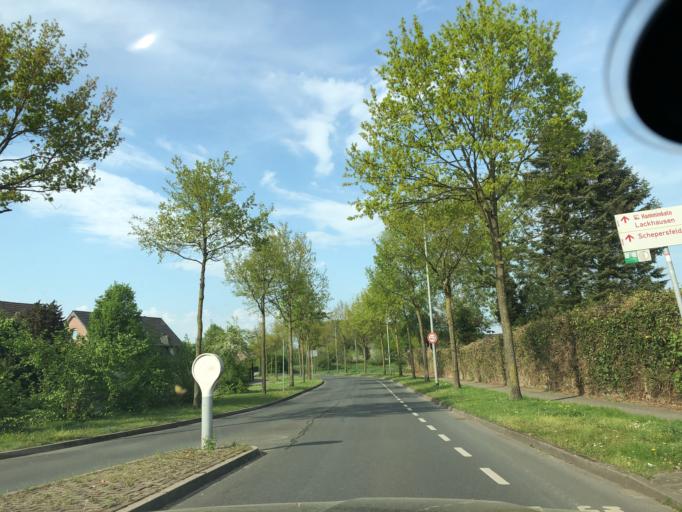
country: DE
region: North Rhine-Westphalia
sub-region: Regierungsbezirk Dusseldorf
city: Wesel
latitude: 51.6526
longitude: 6.6366
